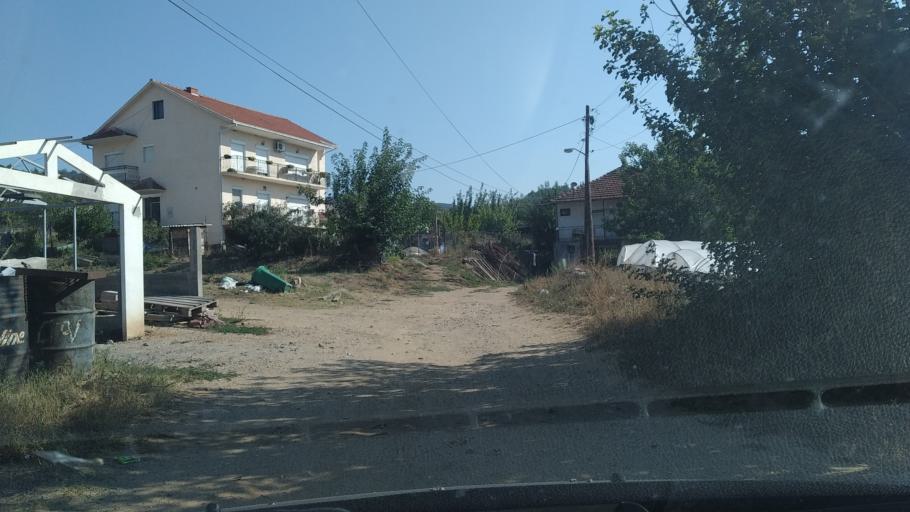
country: MK
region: Bogdanci
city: Bogdanci
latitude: 41.2066
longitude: 22.5825
